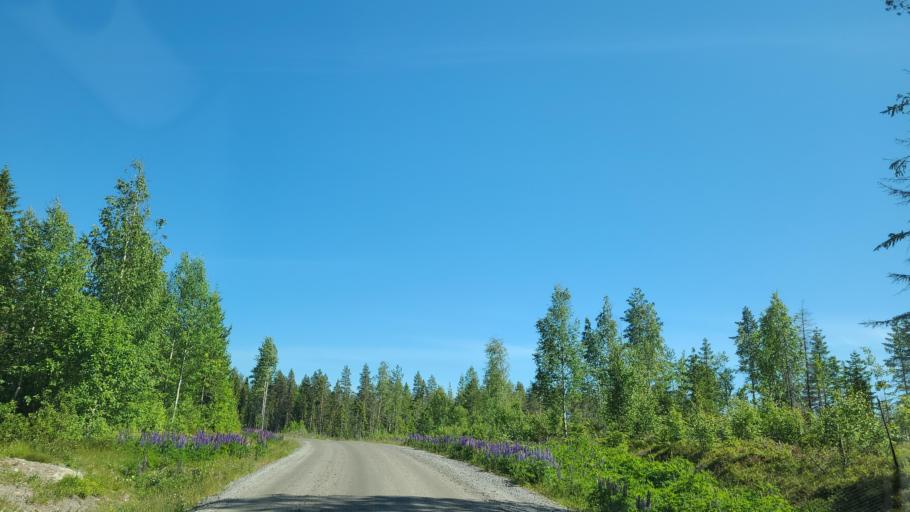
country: SE
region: Vaesterbotten
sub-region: Bjurholms Kommun
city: Bjurholm
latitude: 63.6410
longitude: 19.1042
